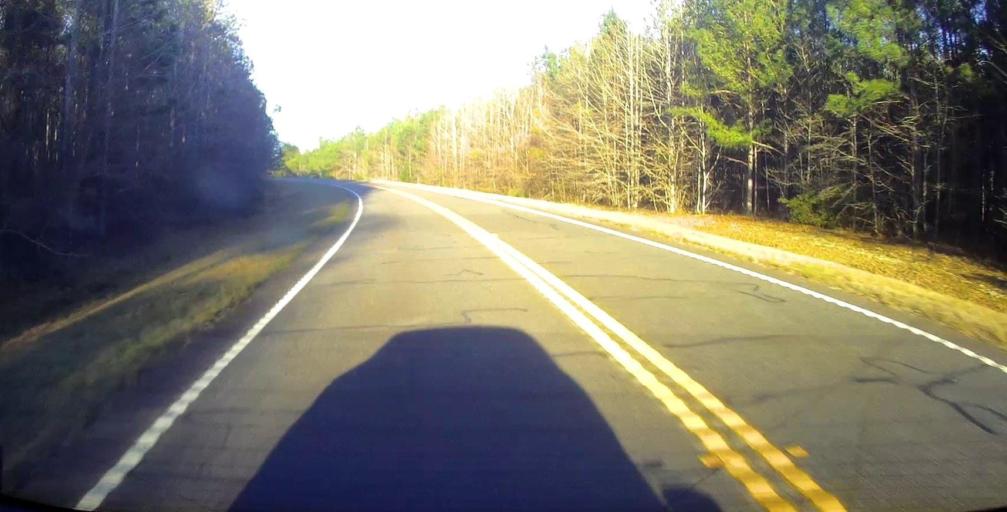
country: US
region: Georgia
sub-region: Talbot County
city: Talbotton
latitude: 32.6493
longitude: -84.6765
